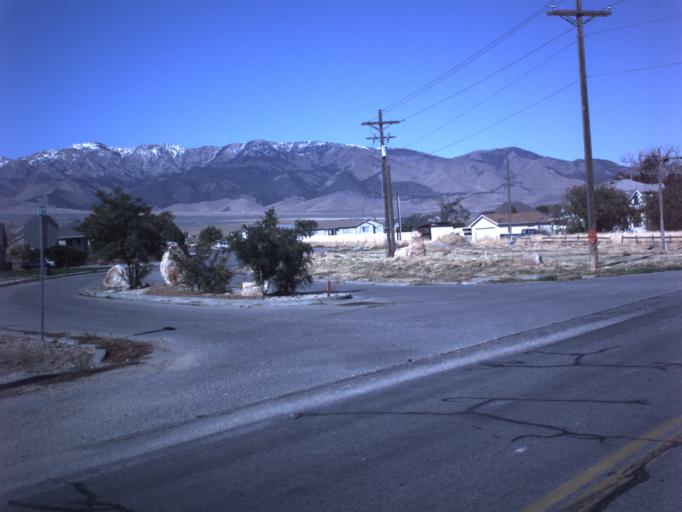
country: US
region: Utah
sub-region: Tooele County
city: Grantsville
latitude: 40.6021
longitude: -112.4844
